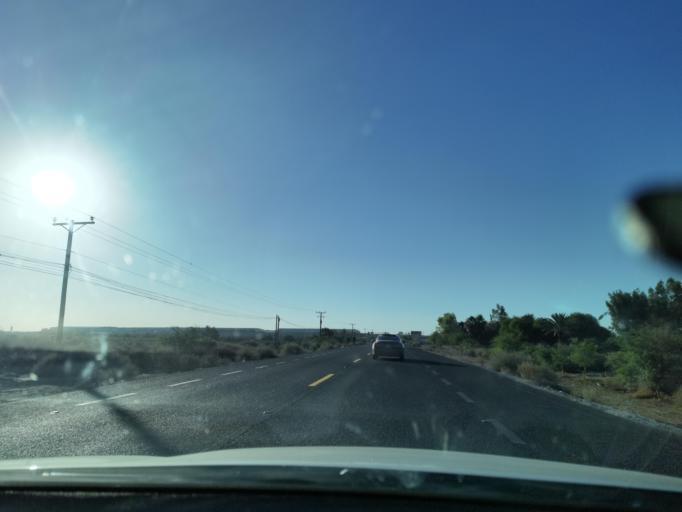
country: MX
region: Baja California
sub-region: Mexicali
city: Islas Agrarias Grupo A
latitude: 32.6388
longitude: -115.2928
